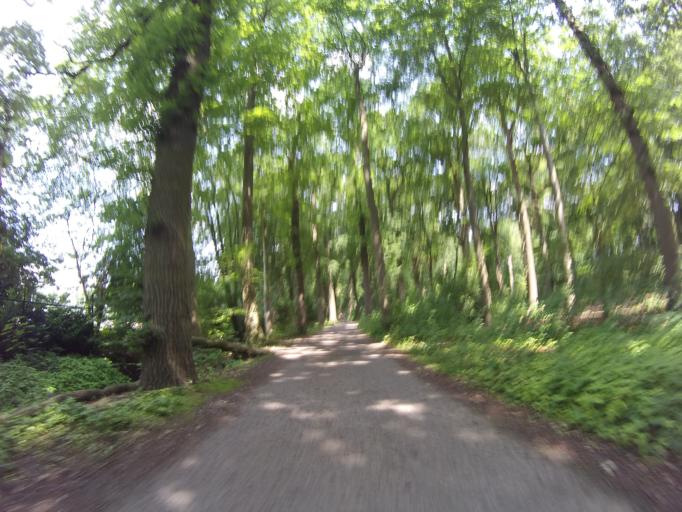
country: NL
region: Utrecht
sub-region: Gemeente De Bilt
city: De Bilt
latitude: 52.1293
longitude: 5.1574
